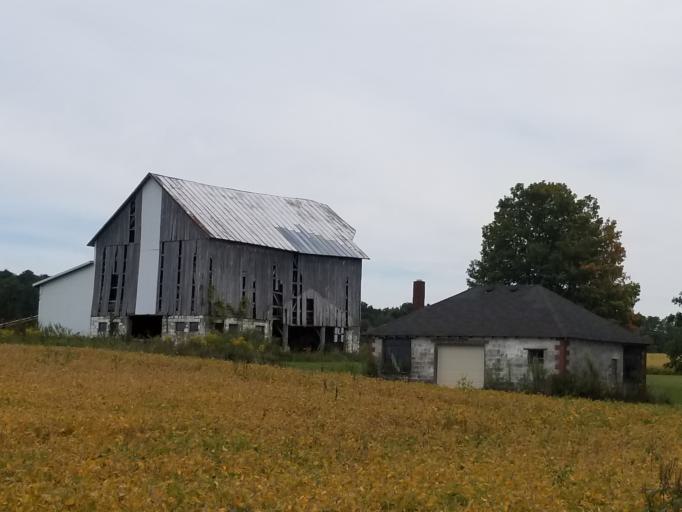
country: US
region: Ohio
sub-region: Knox County
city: Centerburg
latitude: 40.3389
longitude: -82.7068
